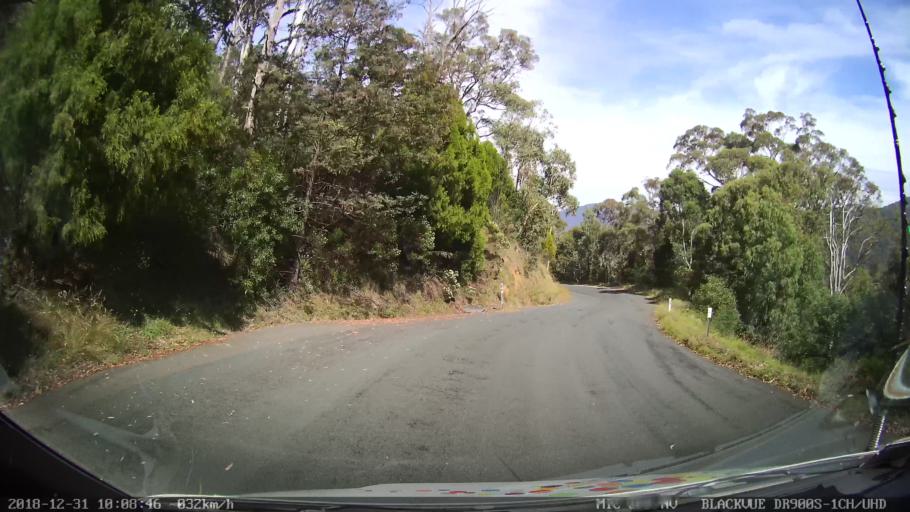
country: AU
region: New South Wales
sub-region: Snowy River
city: Jindabyne
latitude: -36.5359
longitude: 148.1793
